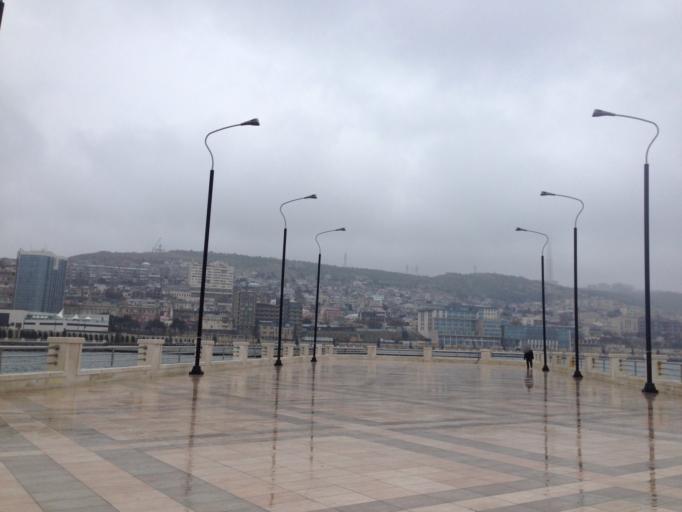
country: AZ
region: Baki
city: Badamdar
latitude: 40.3486
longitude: 49.8428
